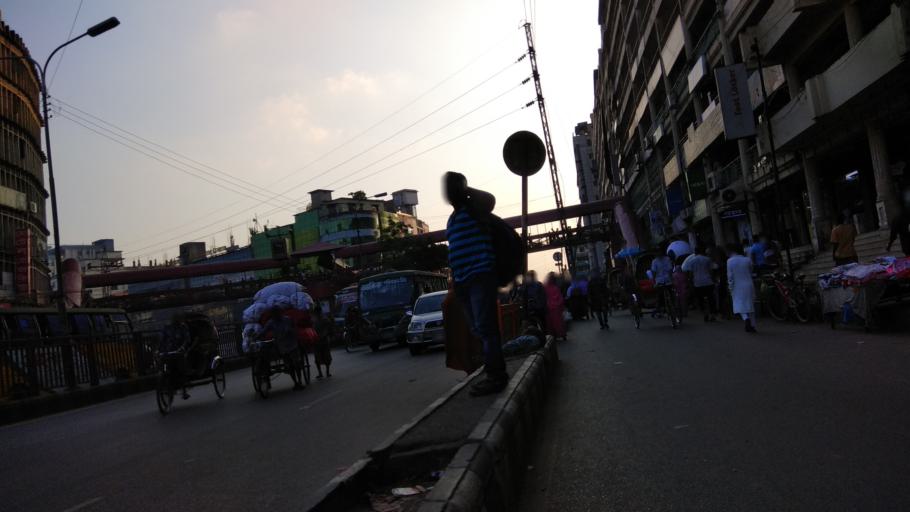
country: BD
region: Dhaka
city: Azimpur
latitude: 23.7995
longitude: 90.3541
